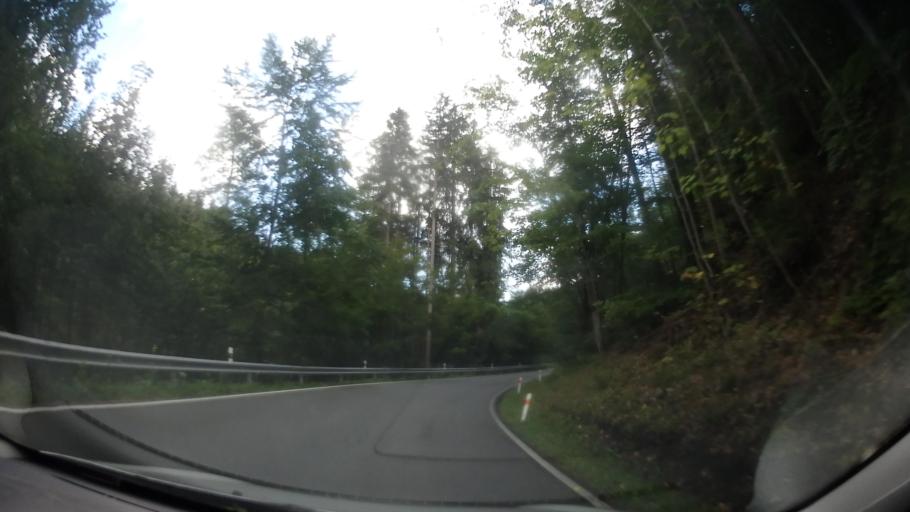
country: CZ
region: Olomoucky
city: Stity
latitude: 49.8831
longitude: 16.7863
